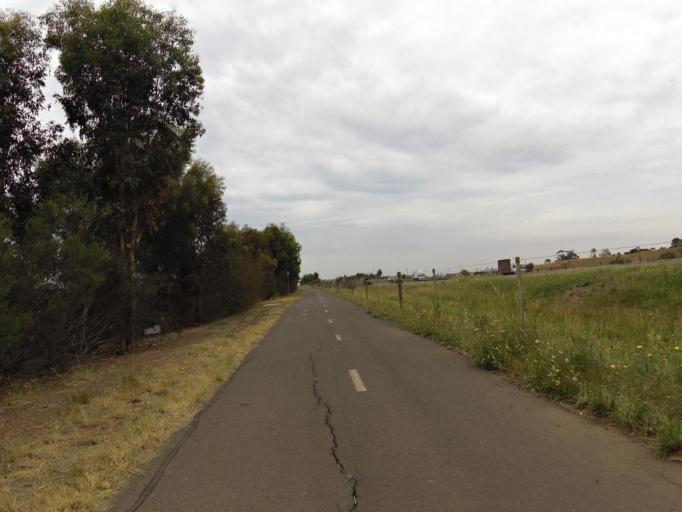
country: AU
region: Victoria
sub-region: Brimbank
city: Derrimut
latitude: -37.7754
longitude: 144.7471
